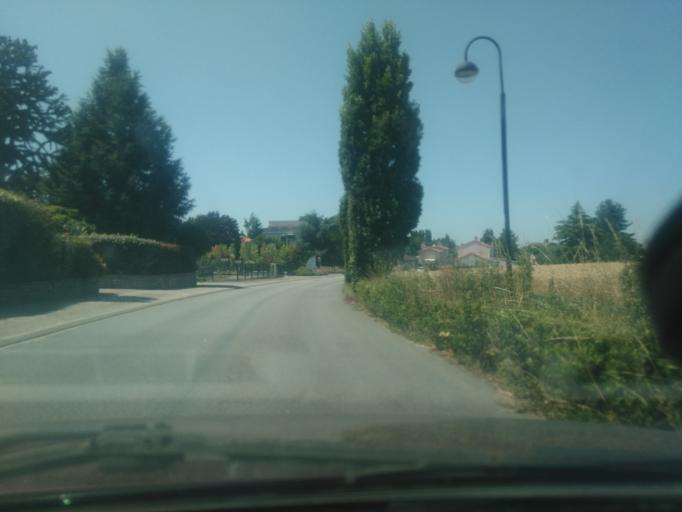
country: FR
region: Pays de la Loire
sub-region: Departement de la Vendee
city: Les Essarts
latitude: 46.7697
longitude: -1.2219
